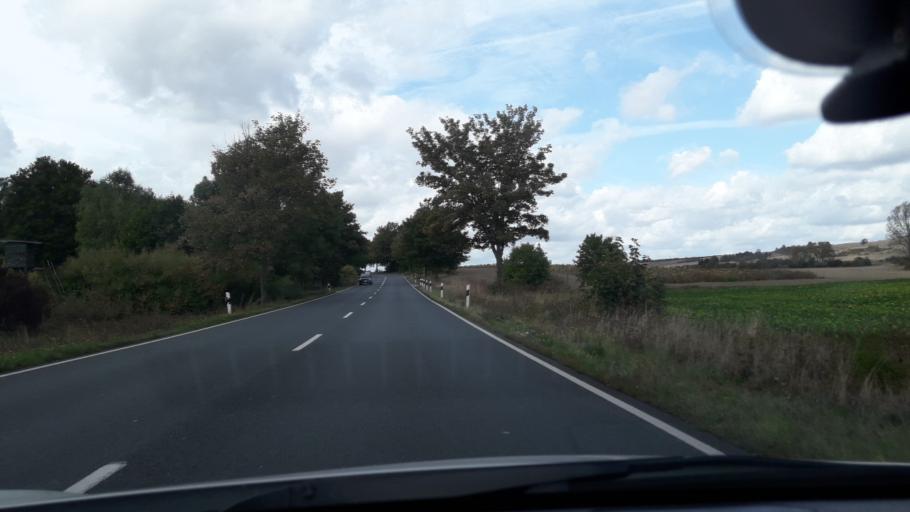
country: DE
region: Lower Saxony
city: Liebenburg
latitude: 52.0156
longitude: 10.3676
